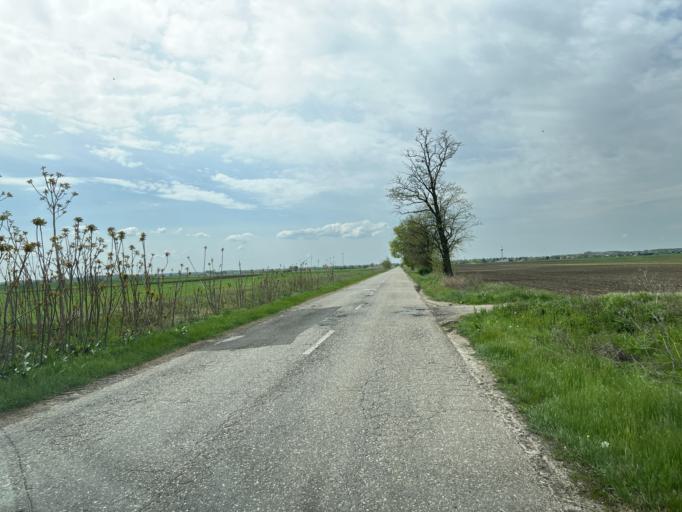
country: HU
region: Pest
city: Tortel
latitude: 47.1374
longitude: 19.9529
